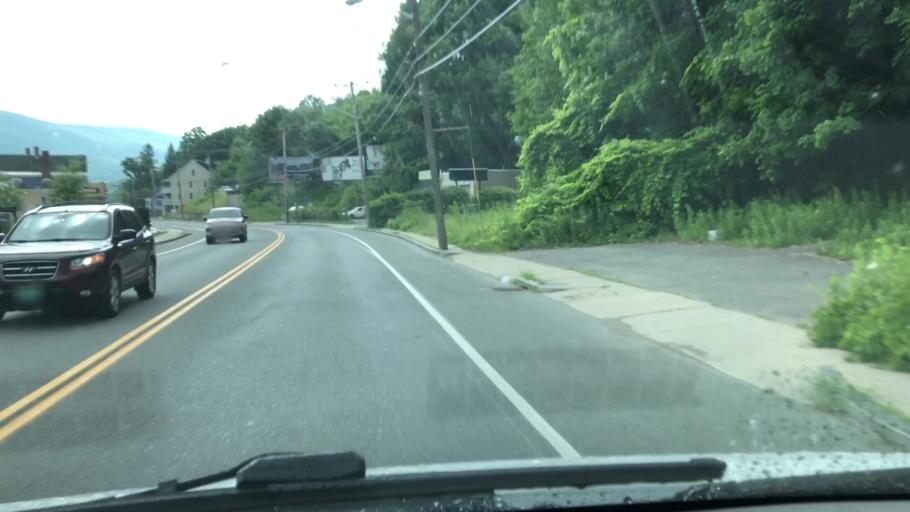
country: US
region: Massachusetts
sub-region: Berkshire County
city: North Adams
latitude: 42.6917
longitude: -73.1143
